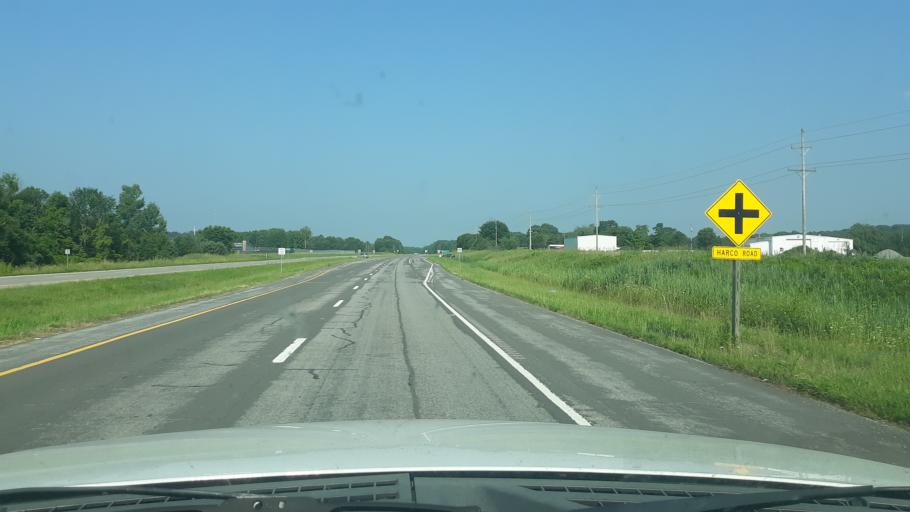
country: US
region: Illinois
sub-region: Saline County
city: Carrier Mills
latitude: 37.7335
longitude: -88.6703
